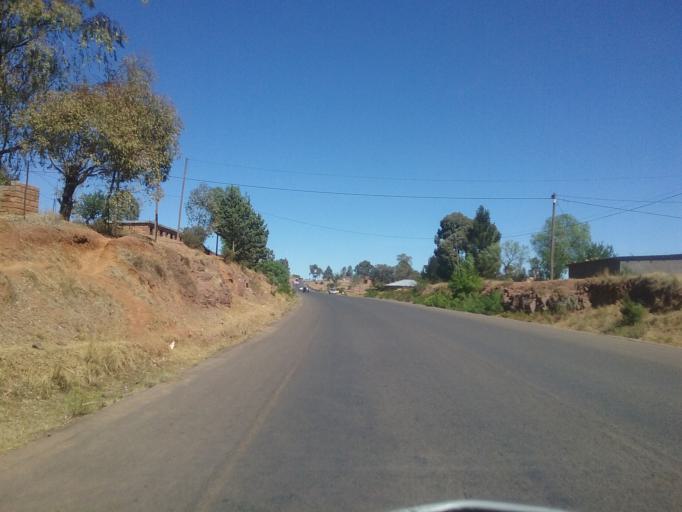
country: LS
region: Quthing
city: Quthing
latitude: -30.3991
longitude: 27.6708
